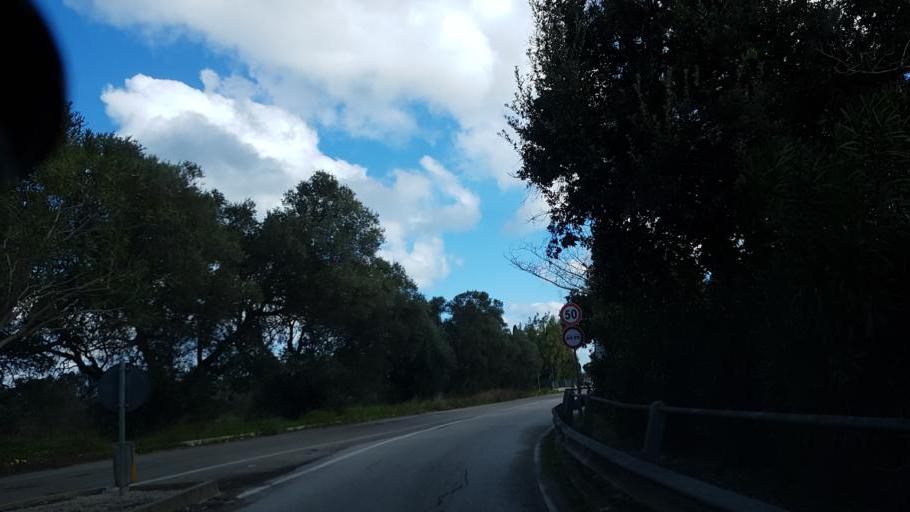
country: IT
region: Apulia
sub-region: Provincia di Brindisi
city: Brindisi
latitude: 40.6351
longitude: 17.9185
